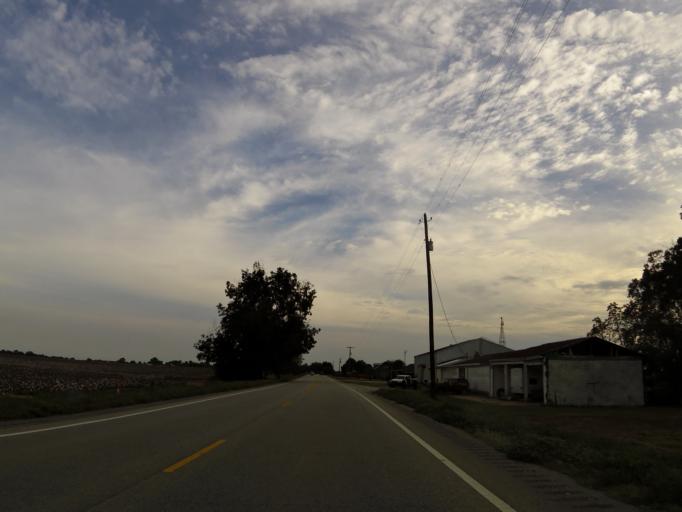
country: US
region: Alabama
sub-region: Monroe County
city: Frisco City
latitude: 31.2873
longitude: -87.5061
